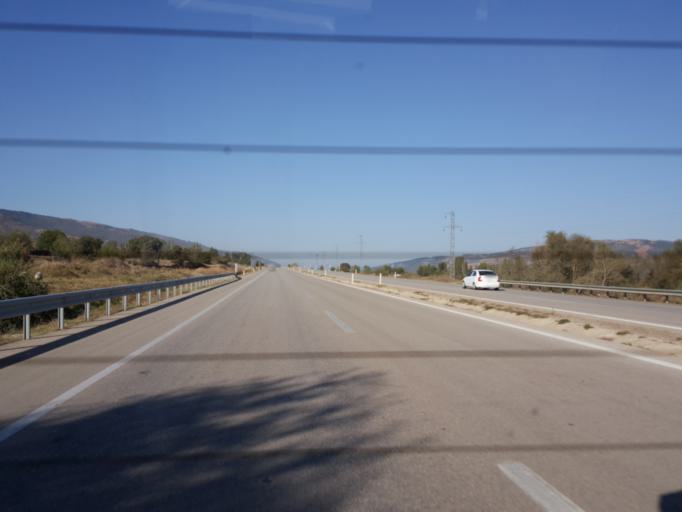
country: TR
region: Amasya
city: Ezinepazari
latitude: 40.5696
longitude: 36.0855
